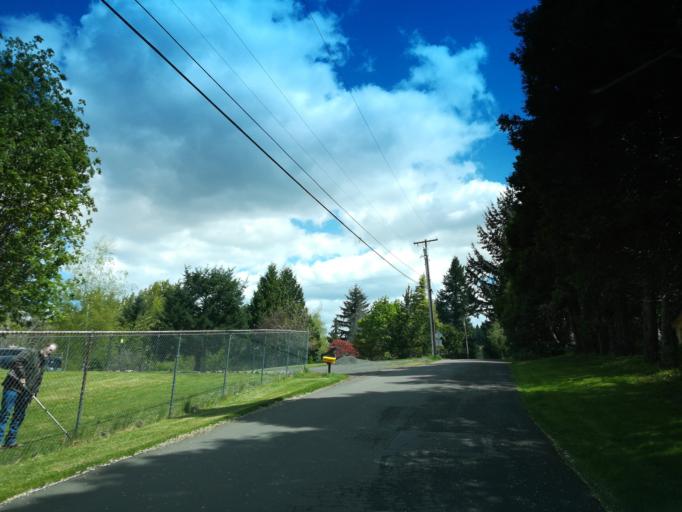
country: US
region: Oregon
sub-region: Clackamas County
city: Damascus
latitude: 45.4277
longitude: -122.4601
